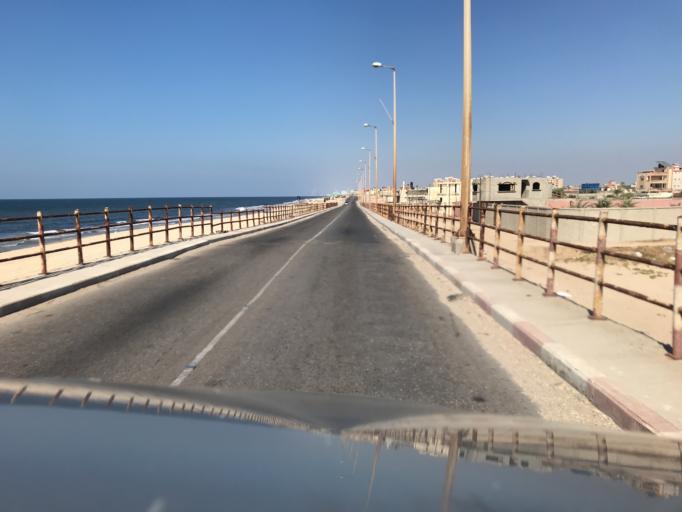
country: PS
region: Gaza Strip
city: An Nusayrat
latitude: 31.4638
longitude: 34.3762
